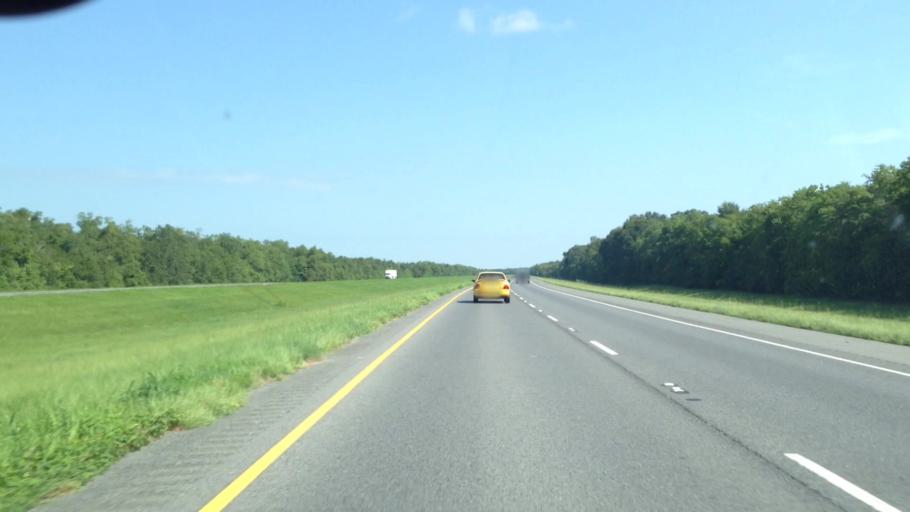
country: US
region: Louisiana
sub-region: Saint Landry Parish
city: Opelousas
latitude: 30.6697
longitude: -92.0717
